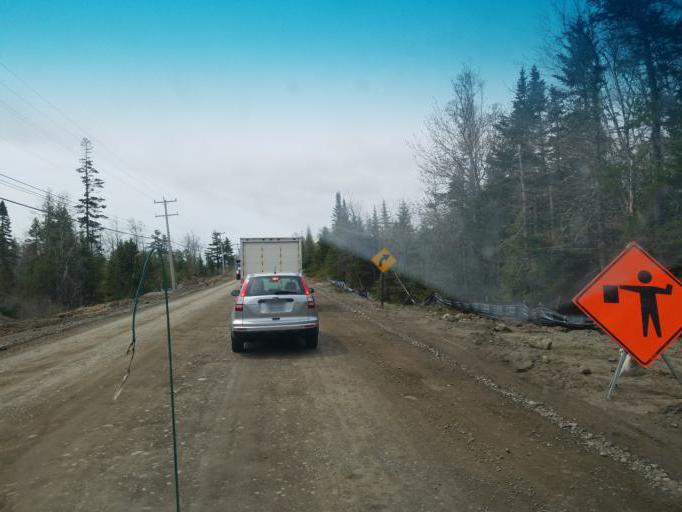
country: US
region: Maine
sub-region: Washington County
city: East Machias
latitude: 44.7707
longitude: -67.1967
